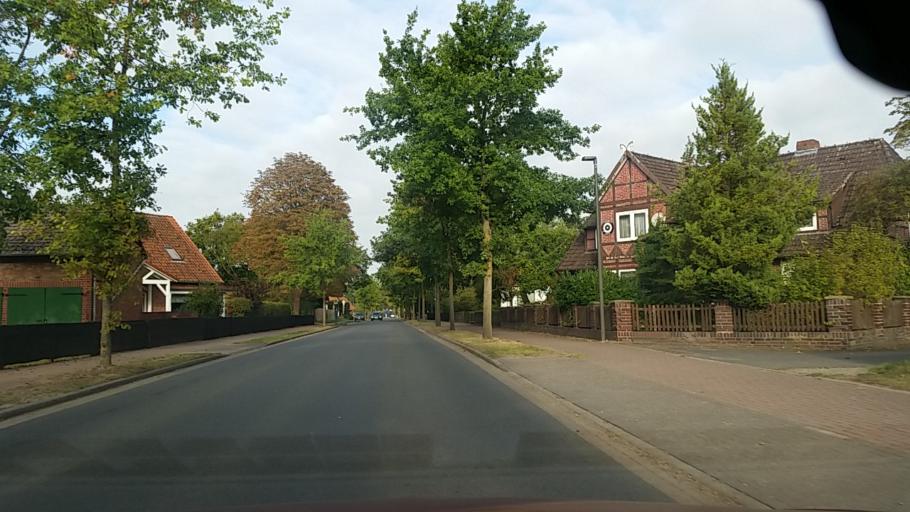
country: DE
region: Lower Saxony
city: Ahnsbeck
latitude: 52.6116
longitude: 10.2834
